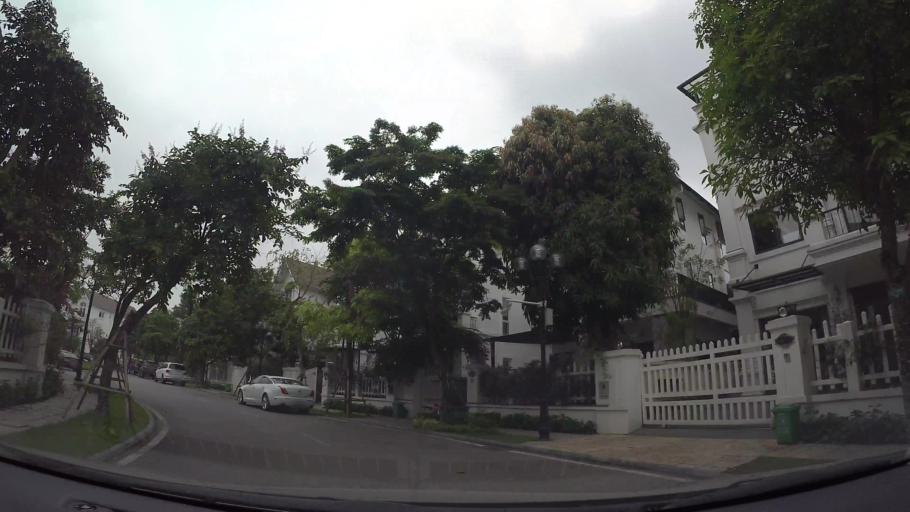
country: VN
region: Ha Noi
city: Trau Quy
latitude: 21.0471
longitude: 105.9151
